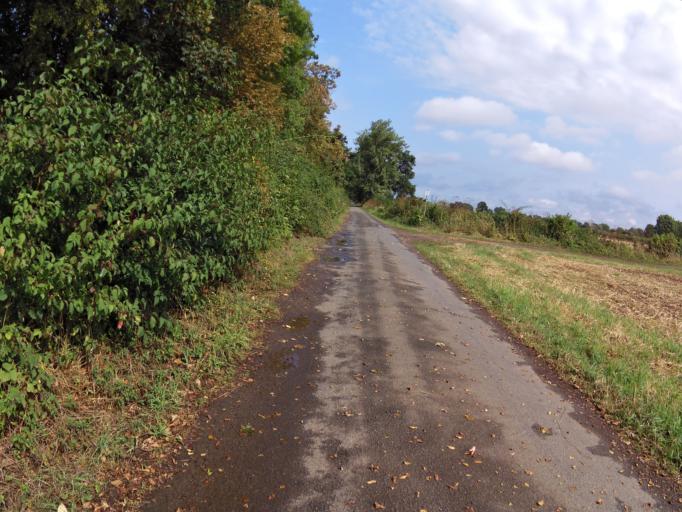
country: DE
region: Lower Saxony
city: Balge
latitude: 52.7088
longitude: 9.1906
